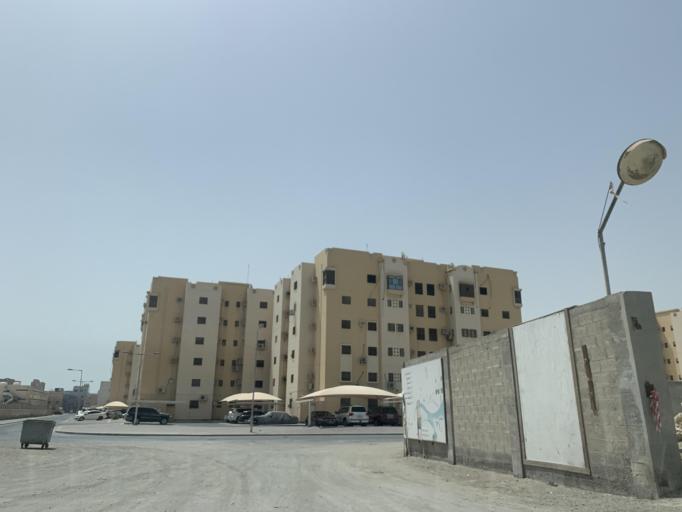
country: BH
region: Northern
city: Sitrah
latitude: 26.1438
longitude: 50.5957
